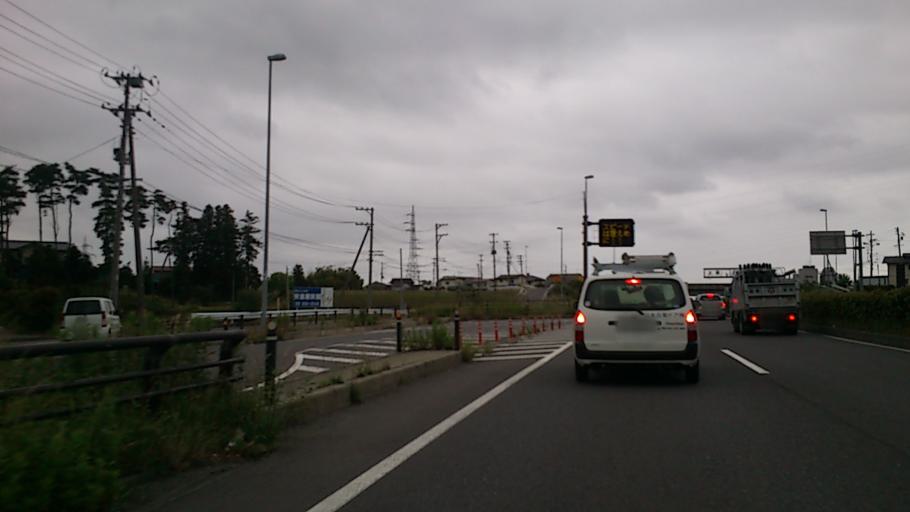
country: JP
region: Fukushima
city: Koriyama
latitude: 37.4538
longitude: 140.3787
